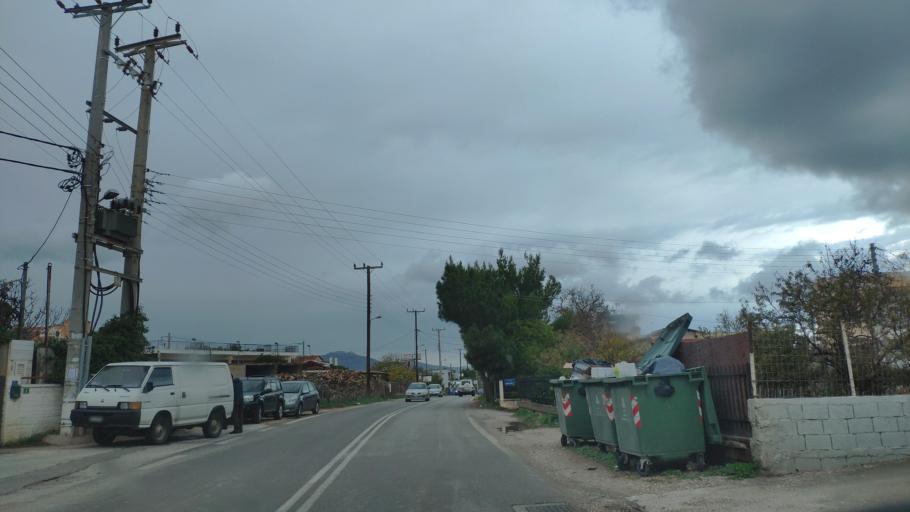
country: GR
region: Attica
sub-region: Nomarchia Anatolikis Attikis
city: Artemida
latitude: 37.9552
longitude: 24.0063
